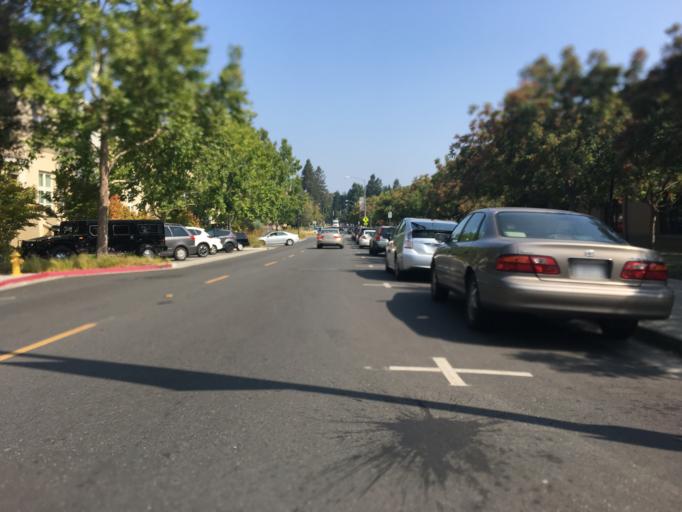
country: US
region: California
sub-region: Santa Clara County
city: Cupertino
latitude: 37.3173
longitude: -122.0293
